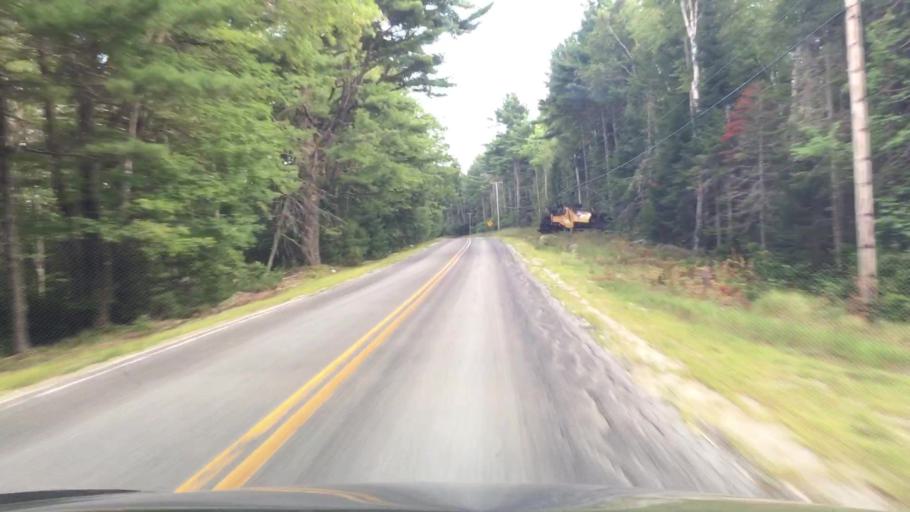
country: US
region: Maine
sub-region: Hancock County
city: Surry
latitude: 44.5099
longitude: -68.5983
